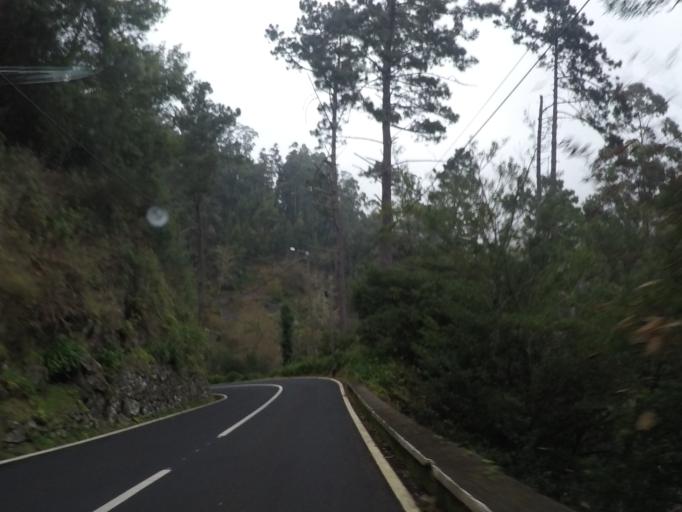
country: PT
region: Madeira
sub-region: Santa Cruz
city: Camacha
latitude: 32.6890
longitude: -16.8519
